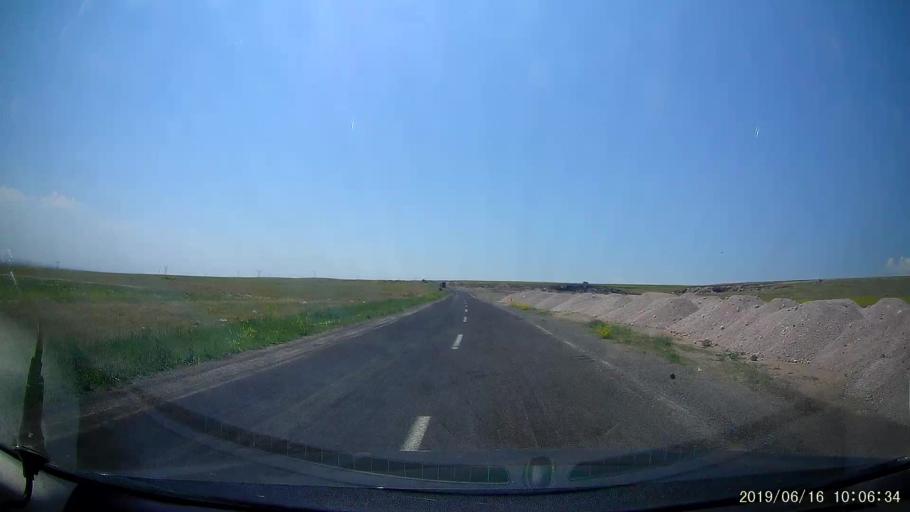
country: TR
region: Kars
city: Digor
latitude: 40.2534
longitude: 43.5439
